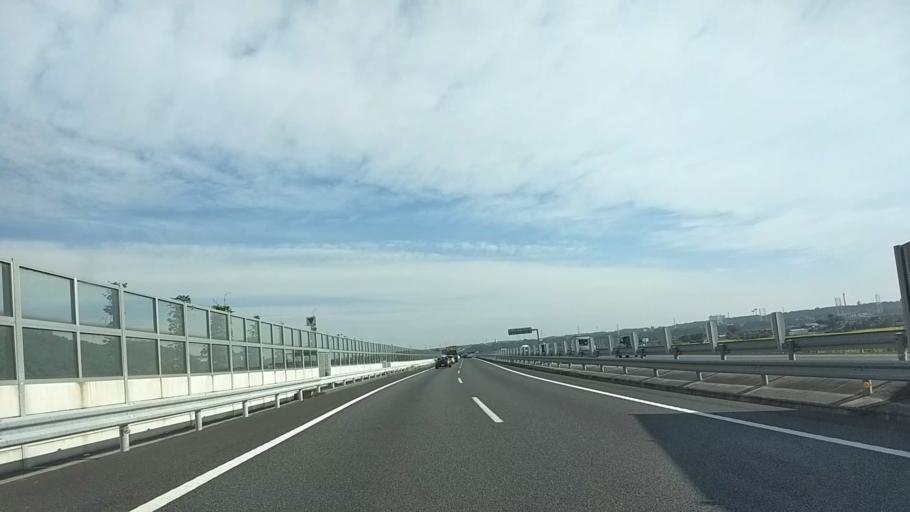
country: JP
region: Kanagawa
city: Zama
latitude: 35.5017
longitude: 139.3657
